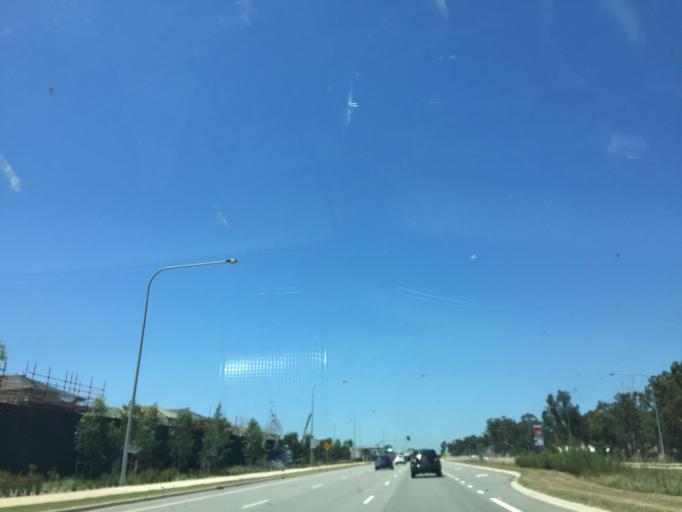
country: AU
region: New South Wales
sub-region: Blacktown
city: Hassall Grove
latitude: -33.7220
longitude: 150.8444
